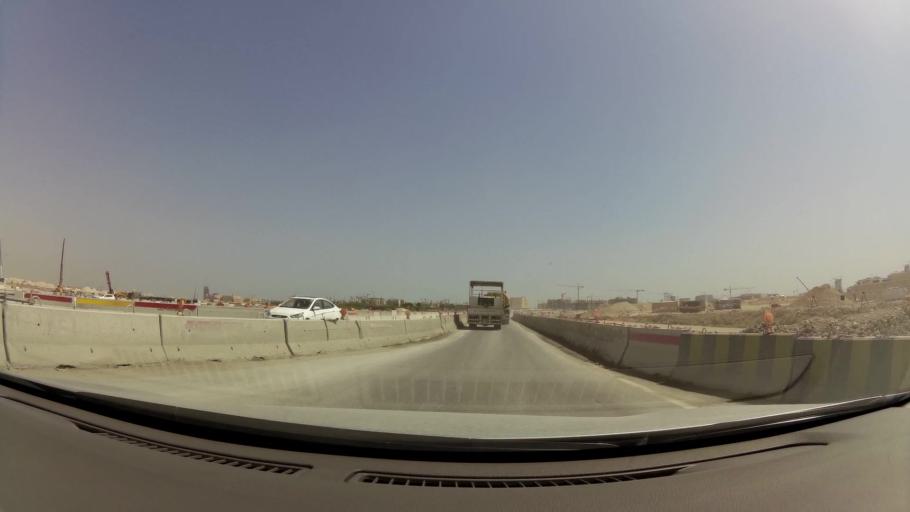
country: QA
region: Baladiyat Umm Salal
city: Umm Salal Muhammad
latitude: 25.4064
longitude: 51.4954
